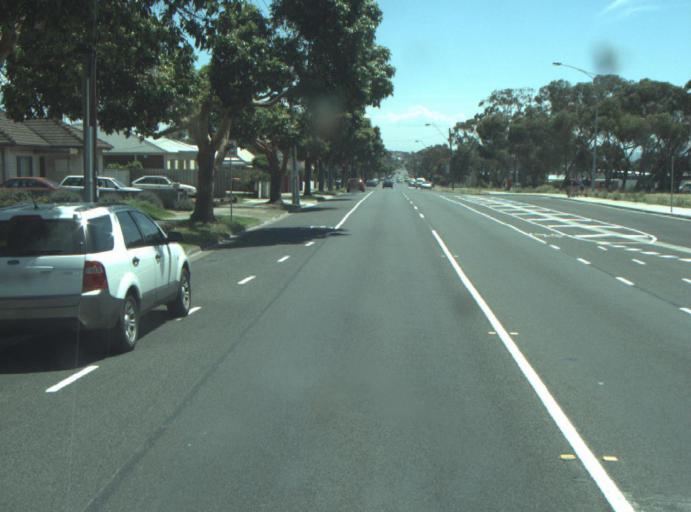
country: AU
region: Victoria
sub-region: Greater Geelong
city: Hamlyn Heights
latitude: -38.1255
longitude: 144.3274
